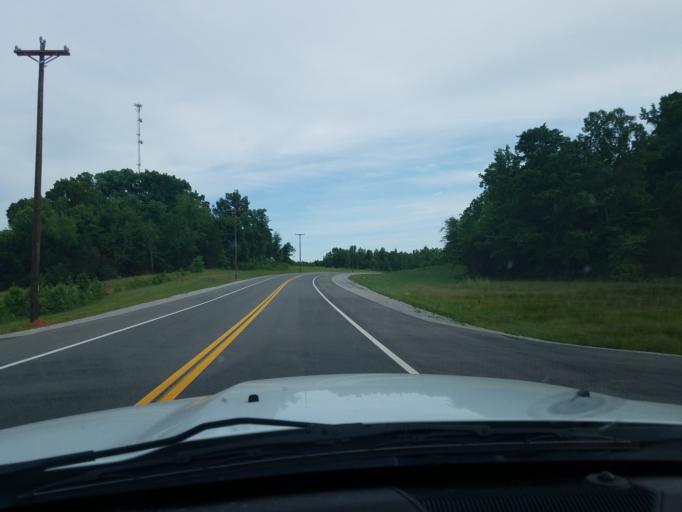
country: US
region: Tennessee
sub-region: Putnam County
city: Cookeville
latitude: 36.1562
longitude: -85.5646
